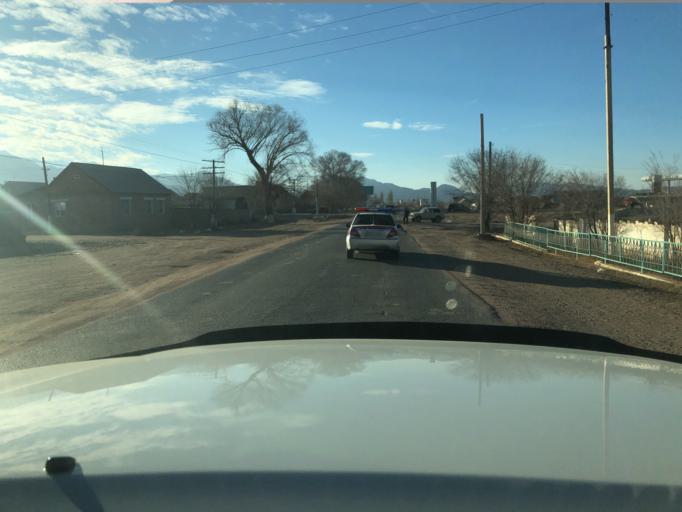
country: KG
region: Ysyk-Koel
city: Bokombayevskoye
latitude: 42.1155
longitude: 76.9828
